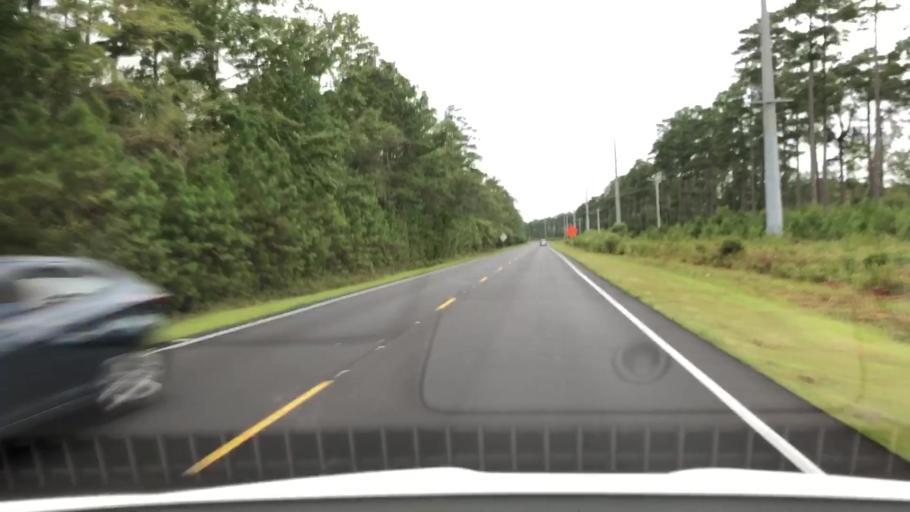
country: US
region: North Carolina
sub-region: Onslow County
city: Swansboro
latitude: 34.7819
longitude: -77.1111
